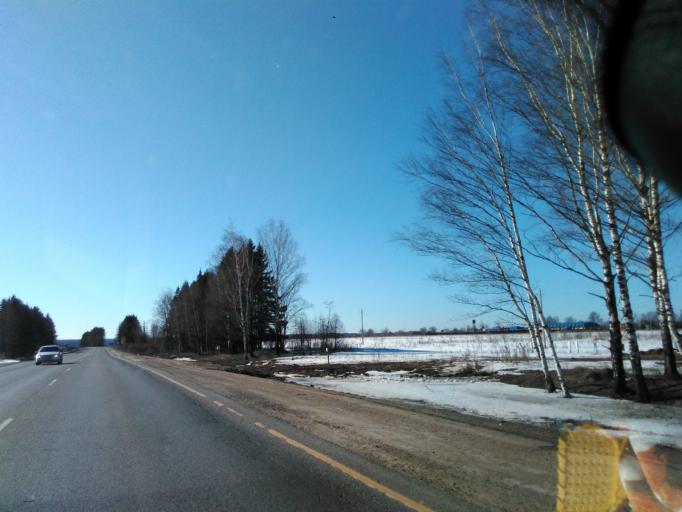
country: RU
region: Moskovskaya
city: Yermolino
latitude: 56.1348
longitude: 37.3853
